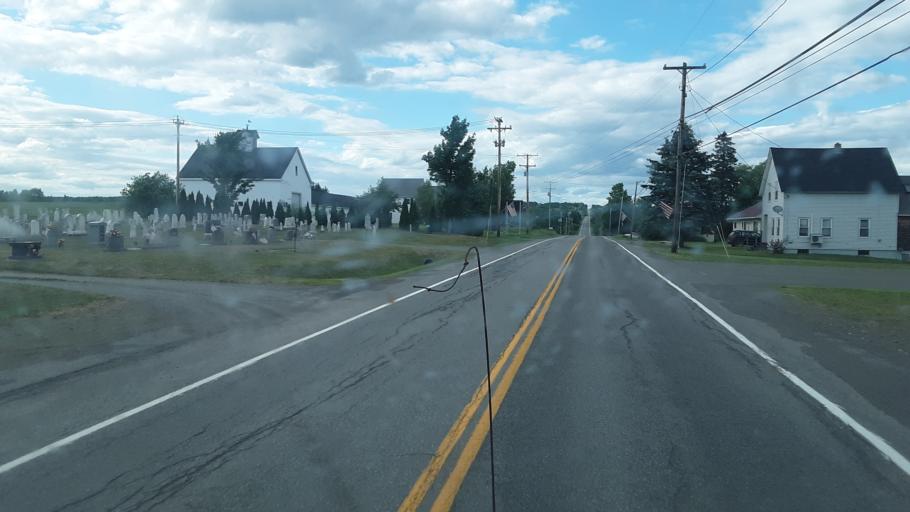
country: US
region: Maine
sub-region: Penobscot County
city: Patten
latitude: 46.0041
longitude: -68.4467
